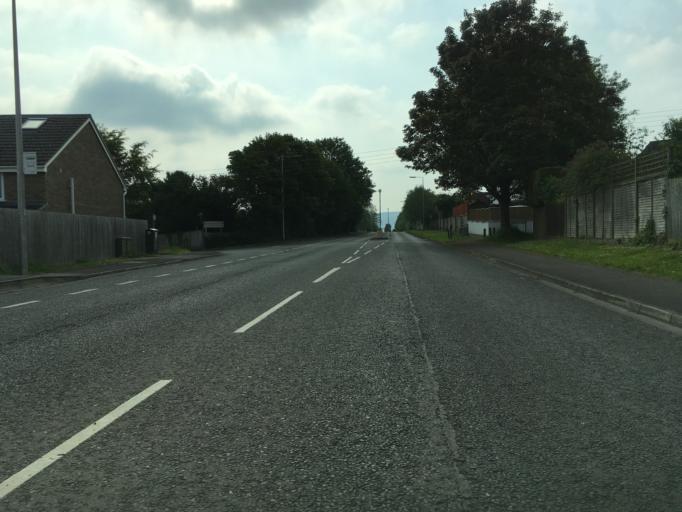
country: GB
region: England
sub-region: North Somerset
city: Nailsea
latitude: 51.4265
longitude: -2.7599
